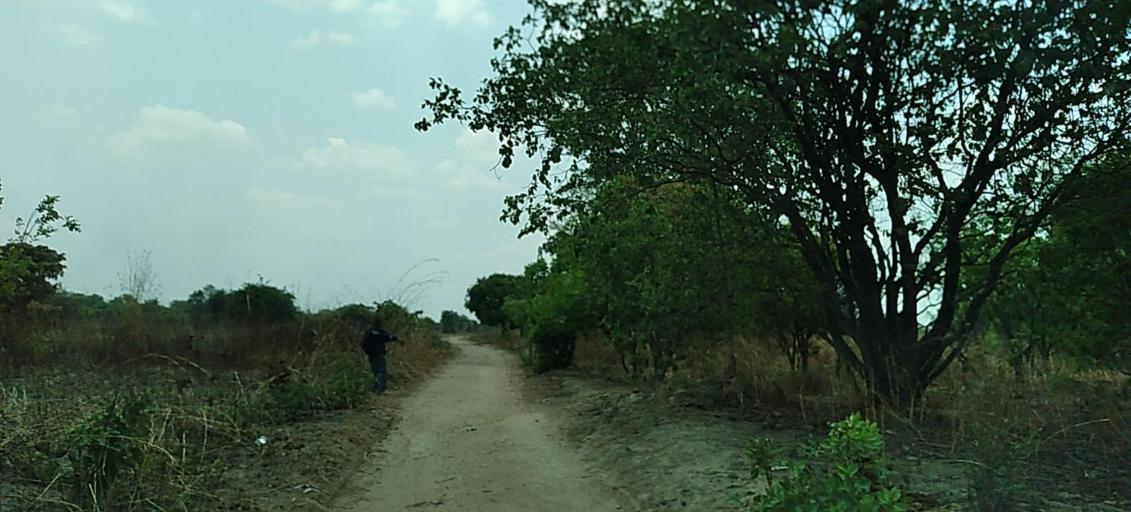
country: ZM
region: Copperbelt
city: Luanshya
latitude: -13.0997
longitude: 28.2997
